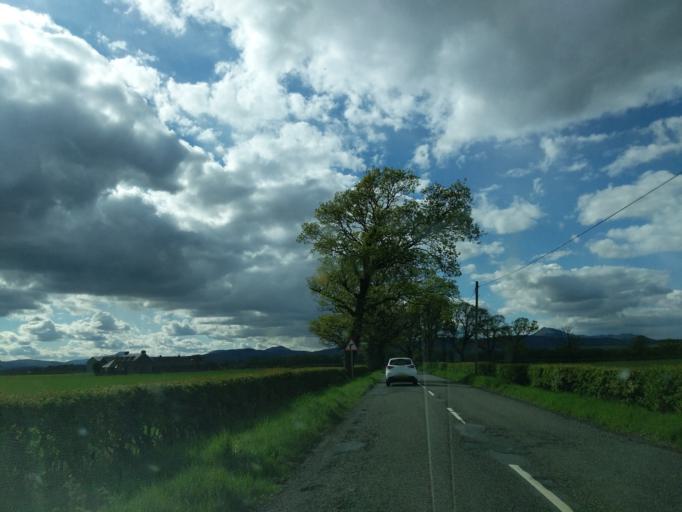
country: GB
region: Scotland
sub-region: Stirling
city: Callander
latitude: 56.1503
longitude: -4.1601
